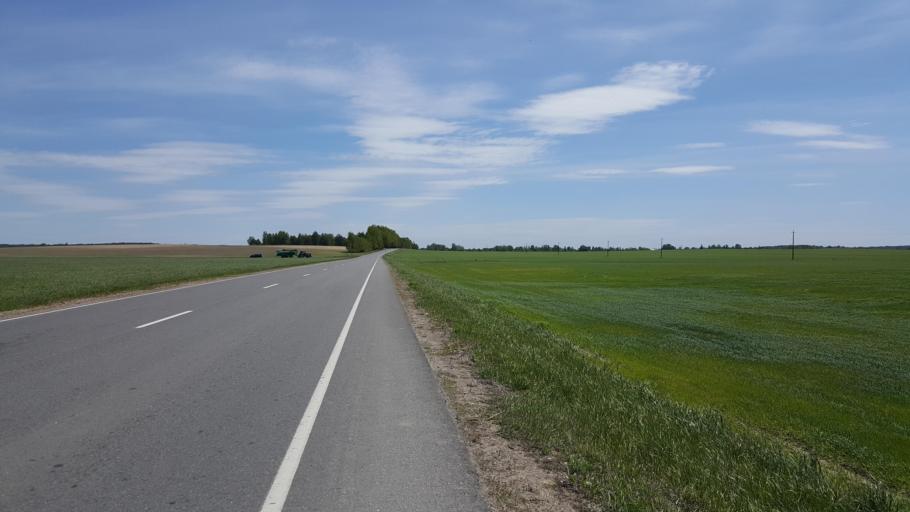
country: BY
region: Brest
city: Zhabinka
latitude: 52.3586
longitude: 24.1630
